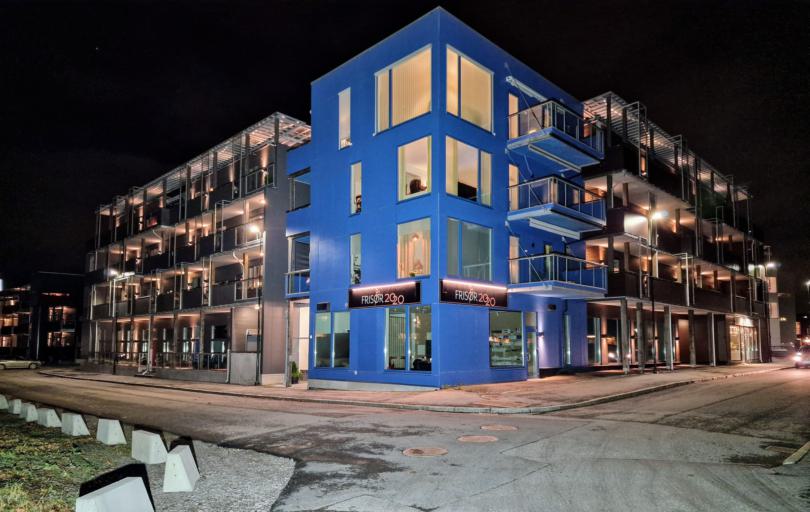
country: NO
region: Akershus
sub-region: Skedsmo
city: Lillestrom
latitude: 60.0037
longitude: 11.0322
